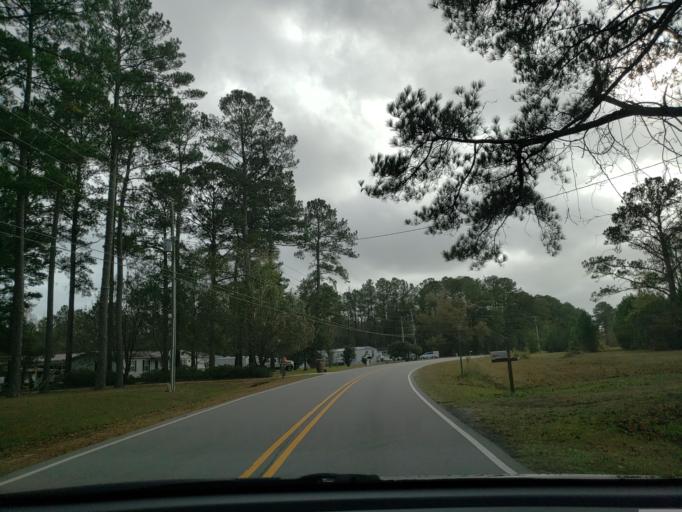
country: US
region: North Carolina
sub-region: Onslow County
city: Jacksonville
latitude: 34.7143
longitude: -77.5780
